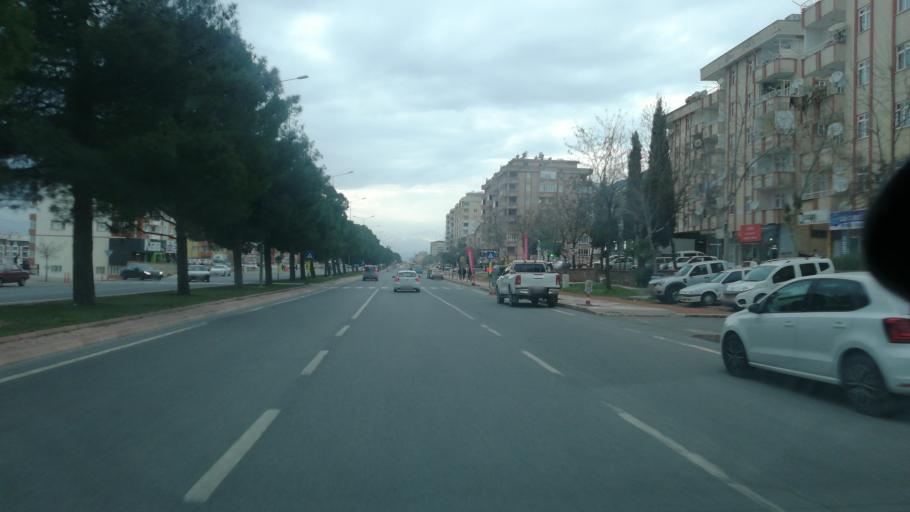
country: TR
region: Kahramanmaras
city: Kahramanmaras
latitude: 37.5939
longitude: 36.8568
